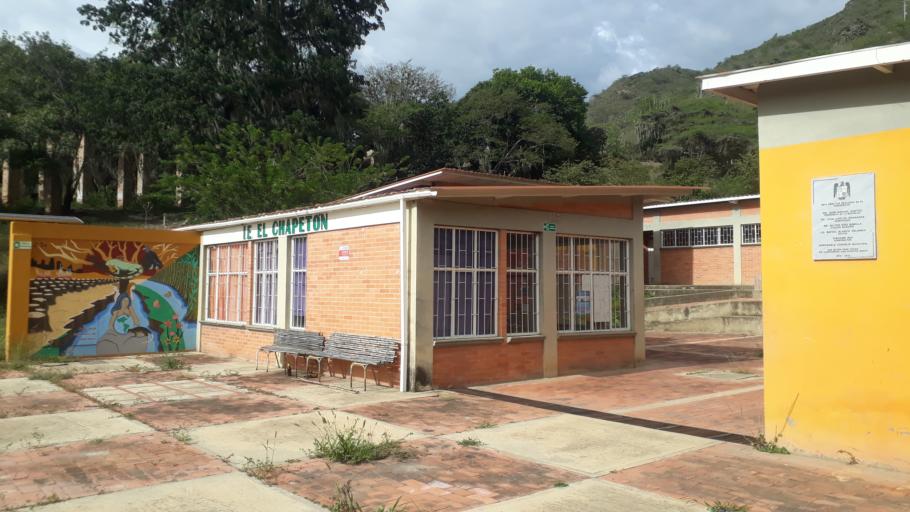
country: CO
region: Boyaca
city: San Mateo
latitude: 6.4481
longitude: -72.6023
